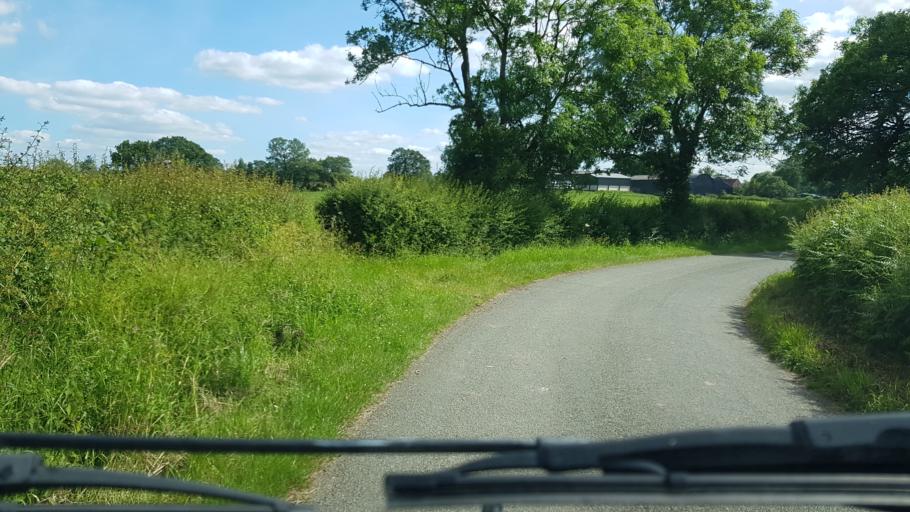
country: GB
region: England
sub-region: Shropshire
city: Romsley
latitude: 52.4550
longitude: -2.2914
